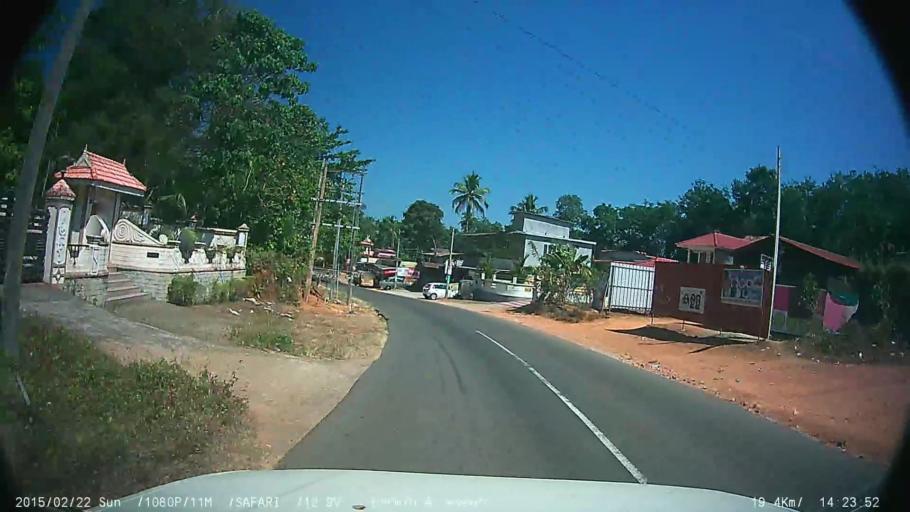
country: IN
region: Kerala
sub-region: Kottayam
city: Lalam
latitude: 9.5675
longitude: 76.7128
